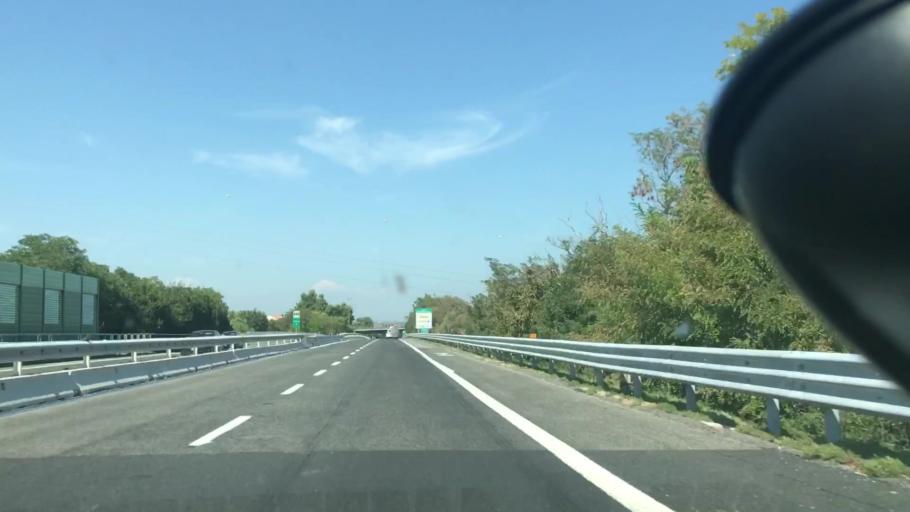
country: IT
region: Abruzzo
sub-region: Provincia di Chieti
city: Vasto
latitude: 42.1344
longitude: 14.6662
